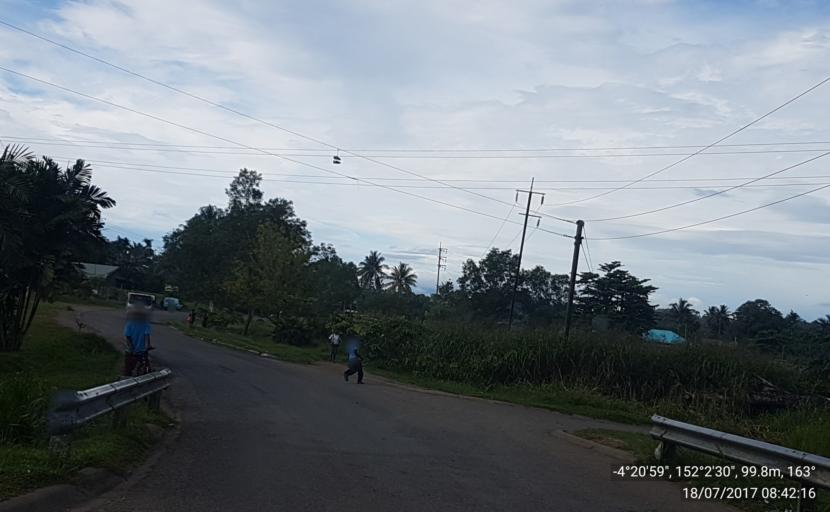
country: PG
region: East New Britain
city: Rabaul
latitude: -4.3496
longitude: 152.0417
